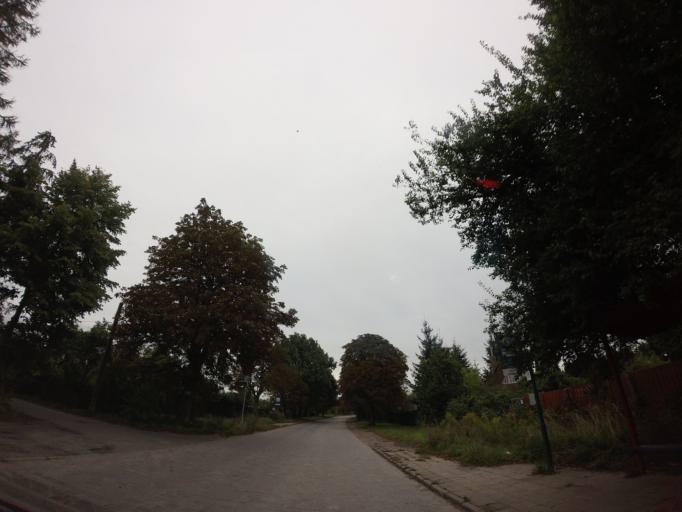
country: PL
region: West Pomeranian Voivodeship
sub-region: Powiat policki
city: Przeclaw
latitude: 53.4418
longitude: 14.4683
